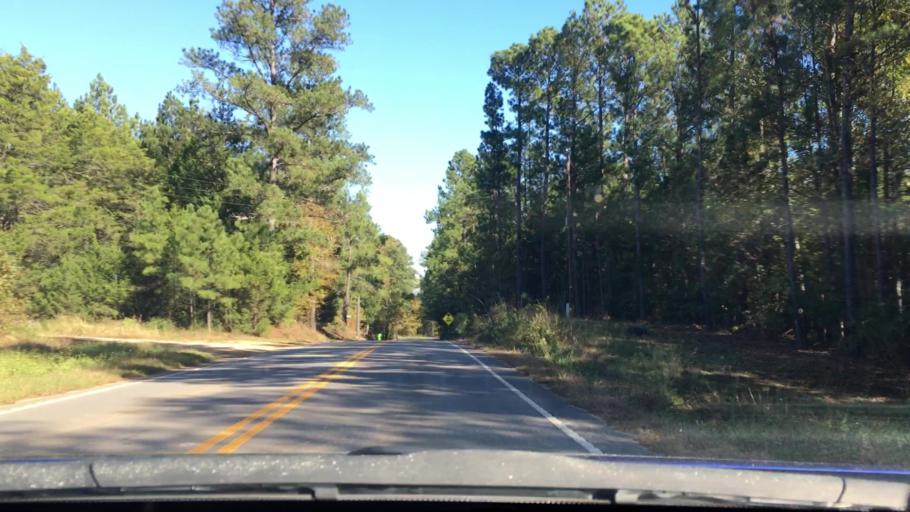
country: US
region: South Carolina
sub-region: Lexington County
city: Irmo
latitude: 34.1109
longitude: -81.1764
